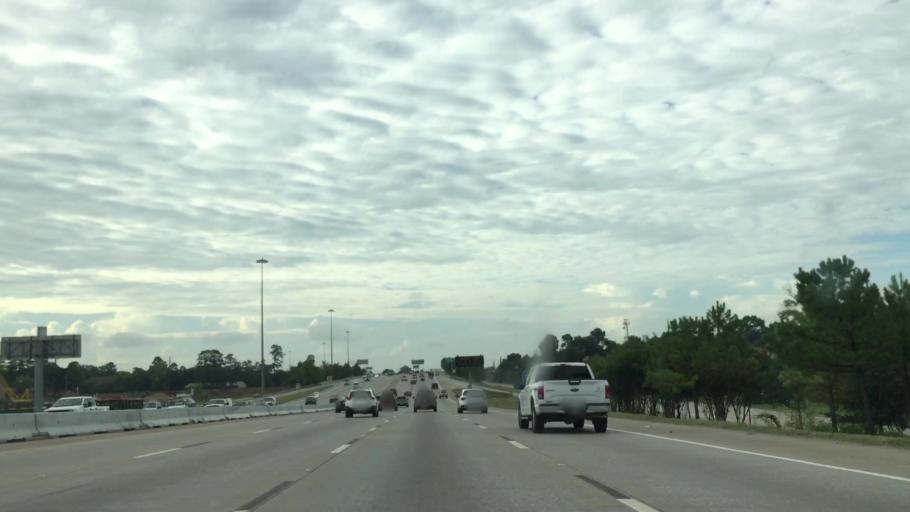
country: US
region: Texas
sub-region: Harris County
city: Oak Cliff Place
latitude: 29.9785
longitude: -95.5664
